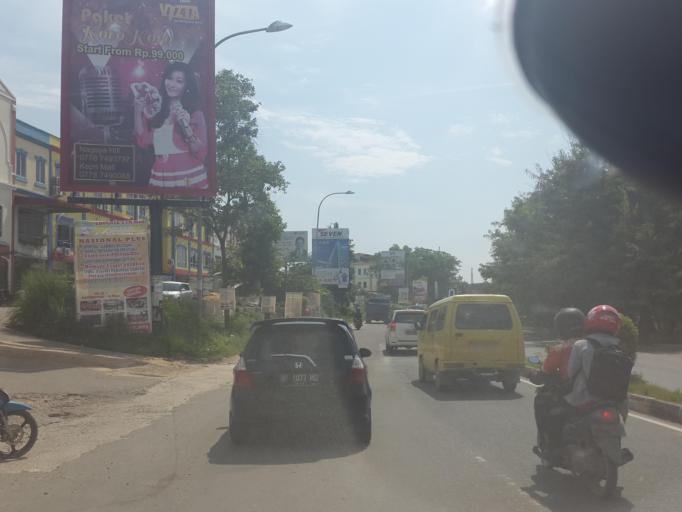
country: SG
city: Singapore
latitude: 1.1192
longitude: 104.0372
